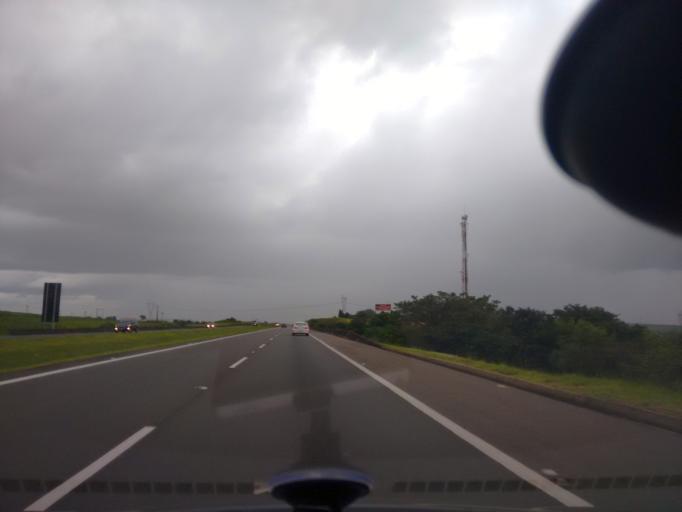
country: BR
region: Sao Paulo
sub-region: Santa Barbara D'Oeste
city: Santa Barbara d'Oeste
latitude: -22.7067
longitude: -47.4570
